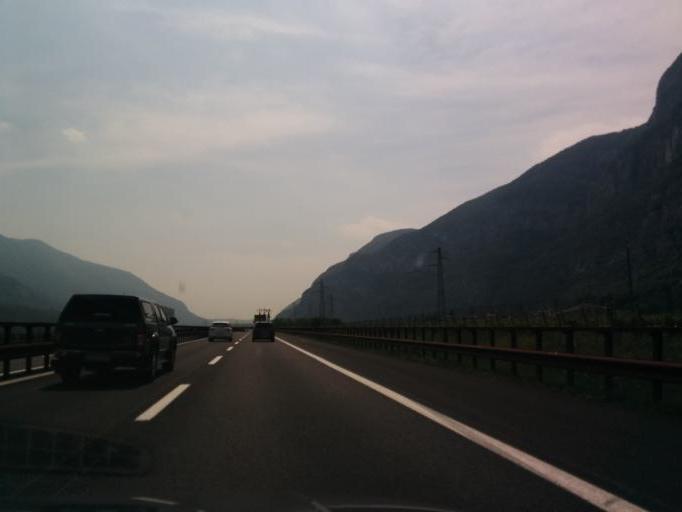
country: IT
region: Veneto
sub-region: Provincia di Verona
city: Dolce
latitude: 45.6289
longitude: 10.8676
